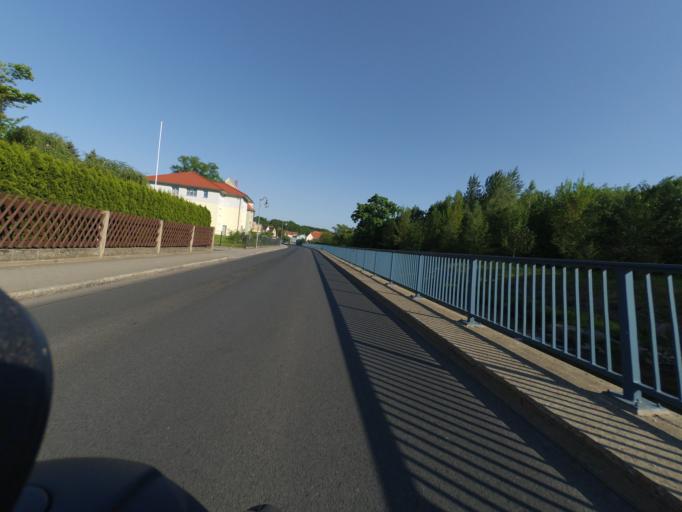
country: DE
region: Saxony
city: Dippoldiswalde
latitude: 50.8952
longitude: 13.6631
